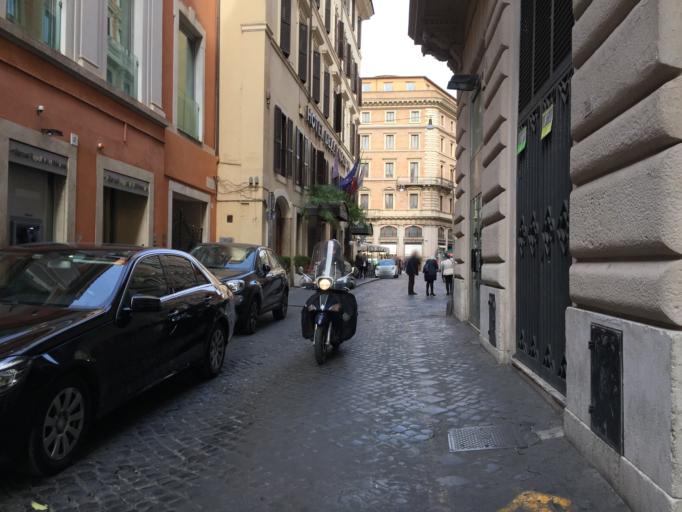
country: VA
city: Vatican City
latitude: 41.9013
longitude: 12.4829
